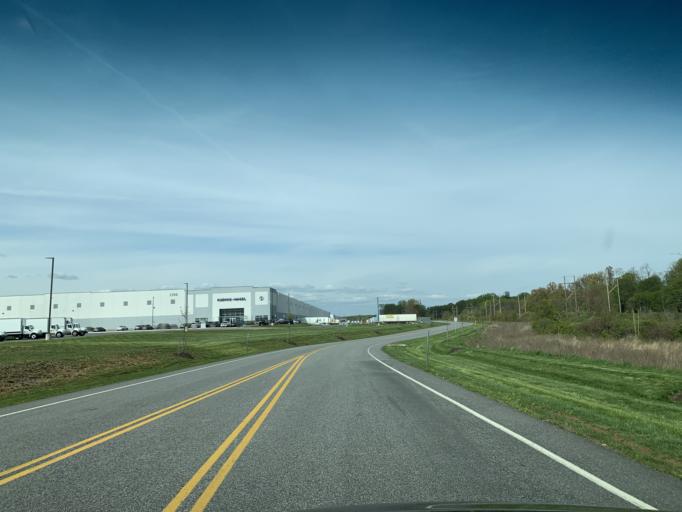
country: US
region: Maryland
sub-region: Harford County
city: Perryman
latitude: 39.4775
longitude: -76.1846
